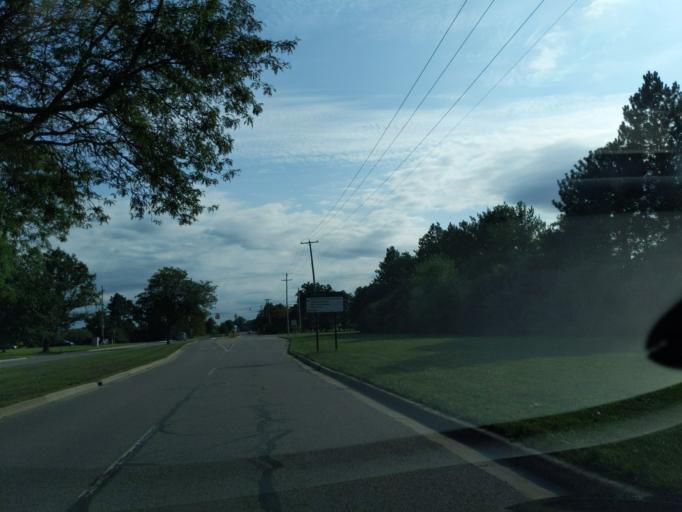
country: US
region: Michigan
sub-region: Ingham County
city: East Lansing
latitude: 42.7131
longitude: -84.4939
